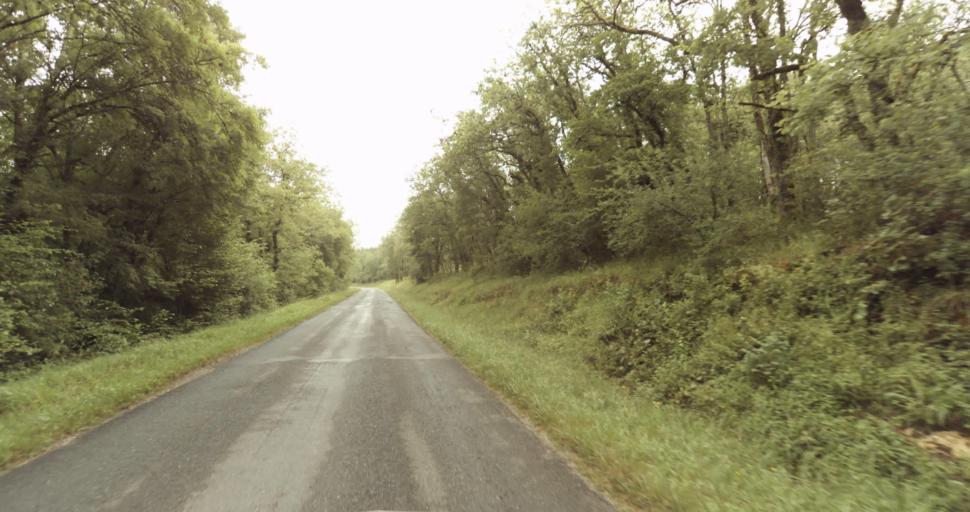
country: FR
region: Aquitaine
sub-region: Departement de la Dordogne
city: Lalinde
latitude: 44.8886
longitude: 0.7728
